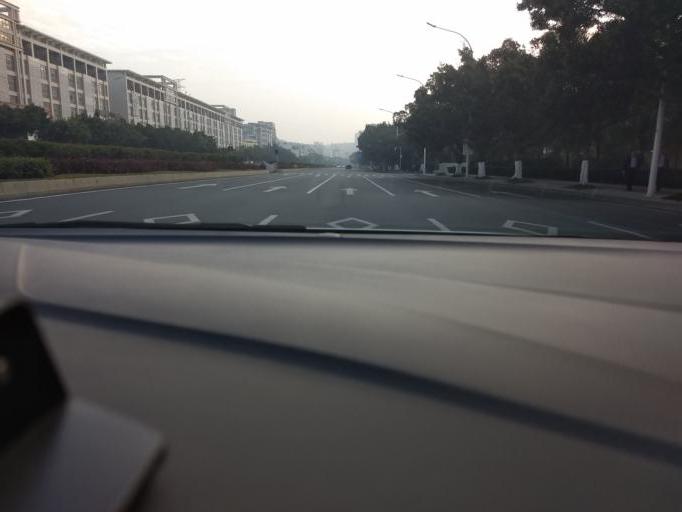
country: CN
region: Guangdong
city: Nansha
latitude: 22.8032
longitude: 113.5369
